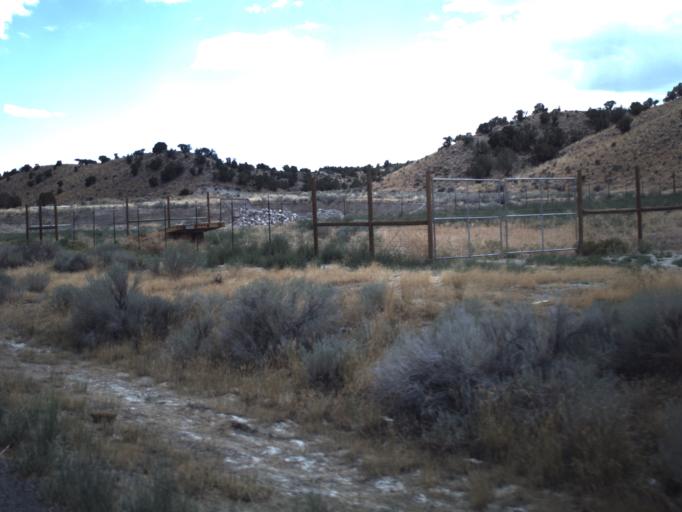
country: US
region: Utah
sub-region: Sanpete County
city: Centerfield
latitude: 39.1334
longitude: -111.7286
